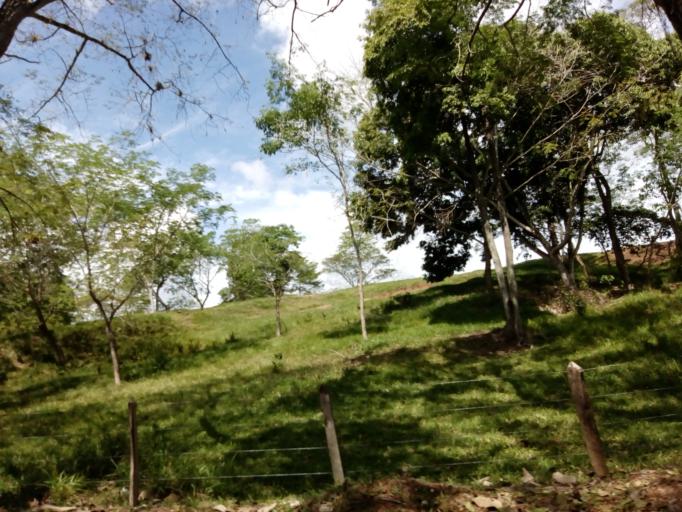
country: CO
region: Boyaca
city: Puerto Boyaca
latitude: 5.9523
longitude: -74.4936
